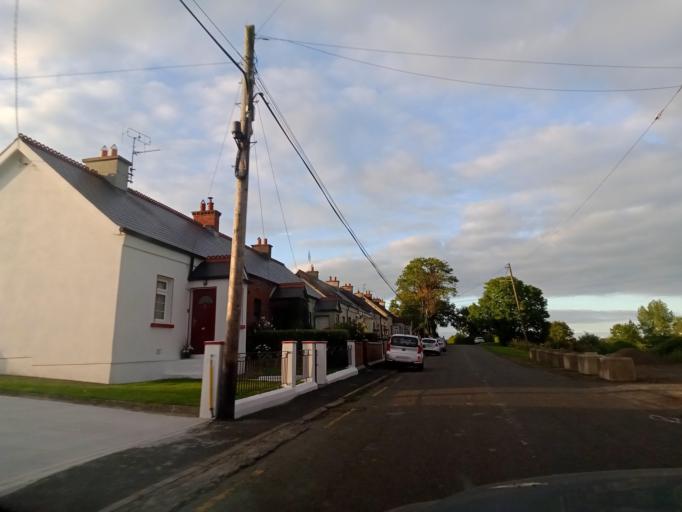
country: IE
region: Leinster
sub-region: Kilkenny
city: Castlecomer
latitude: 52.8290
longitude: -7.2029
